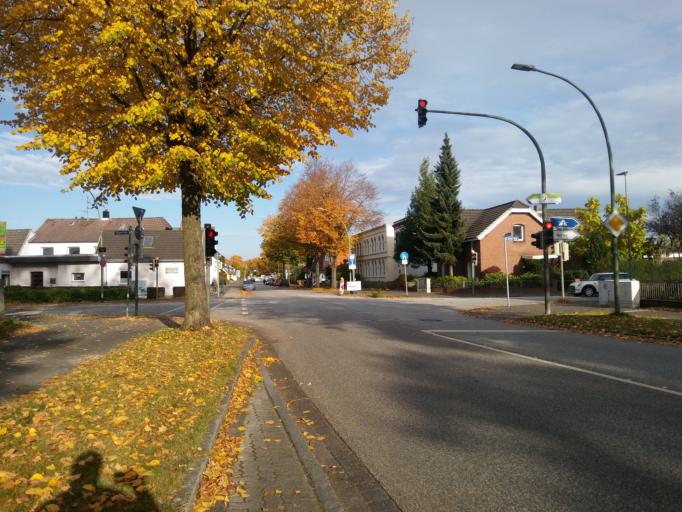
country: DE
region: Schleswig-Holstein
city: Neumunster
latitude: 54.0611
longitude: 9.9739
